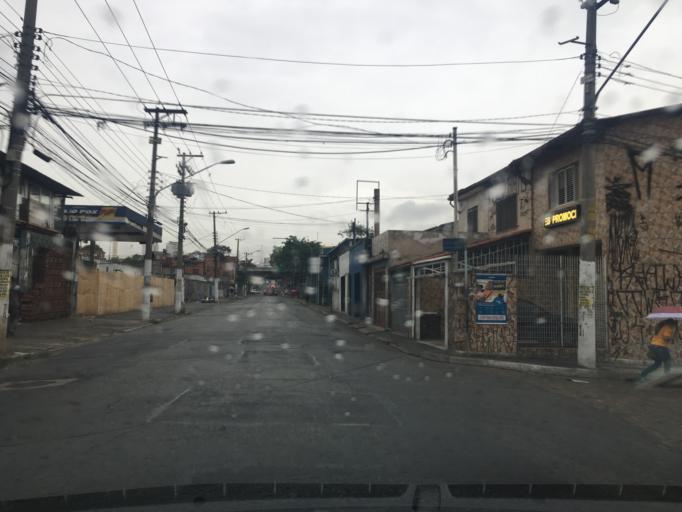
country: BR
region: Sao Paulo
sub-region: Guarulhos
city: Guarulhos
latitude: -23.5134
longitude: -46.5507
